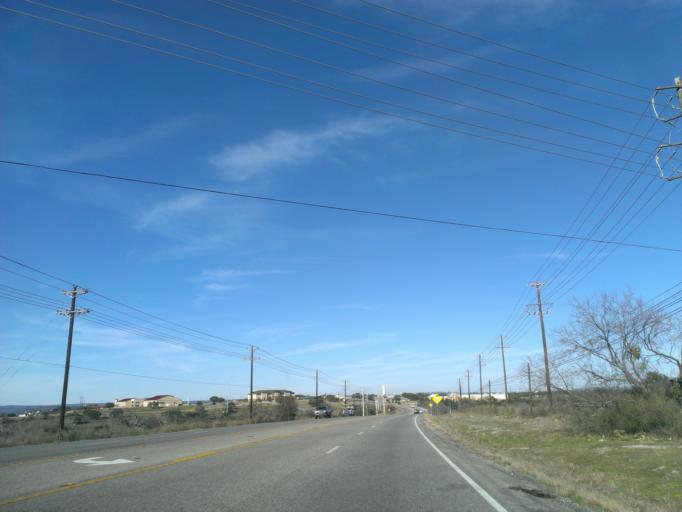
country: US
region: Texas
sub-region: Burnet County
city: Meadowlakes
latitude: 30.5495
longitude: -98.2759
